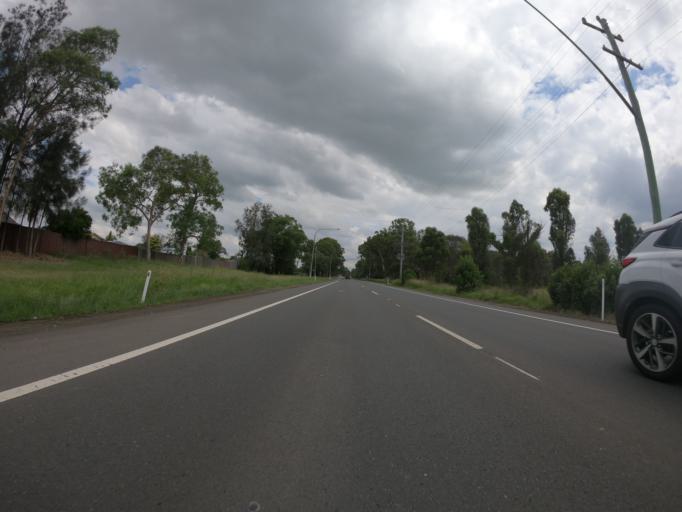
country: AU
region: New South Wales
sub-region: Blacktown
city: Mount Druitt
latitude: -33.7971
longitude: 150.7688
